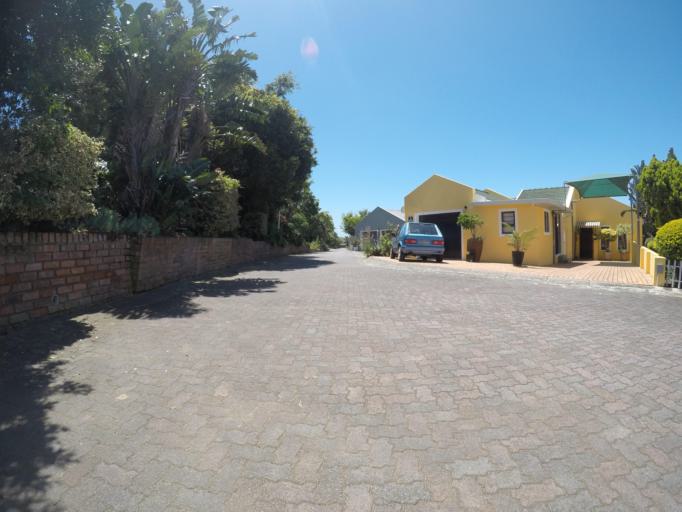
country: ZA
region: Eastern Cape
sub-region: Buffalo City Metropolitan Municipality
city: East London
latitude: -32.9674
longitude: 27.9537
